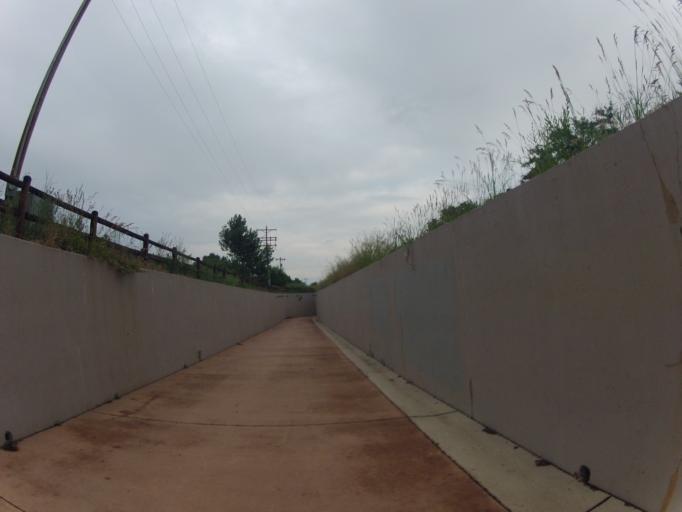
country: US
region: Colorado
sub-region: Larimer County
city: Fort Collins
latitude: 40.5309
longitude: -105.1253
